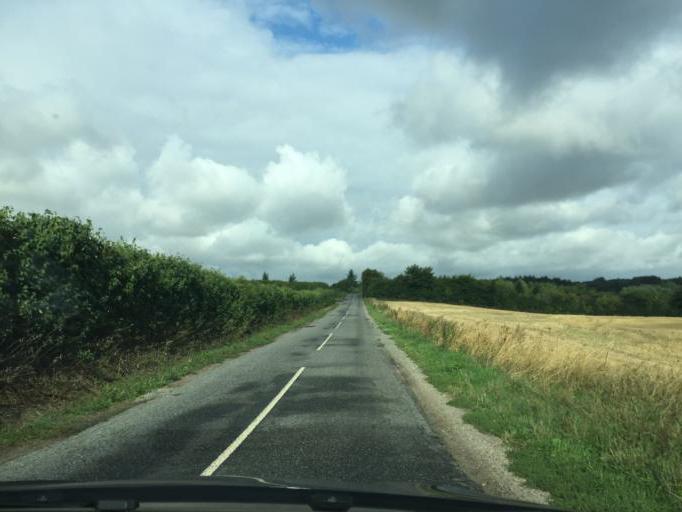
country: DK
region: South Denmark
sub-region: Assens Kommune
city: Harby
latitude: 55.1969
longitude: 10.1904
